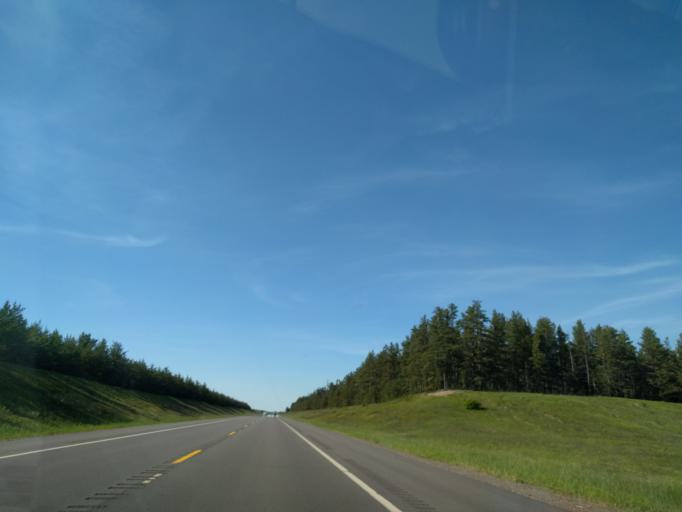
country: US
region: Michigan
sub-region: Marquette County
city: K. I. Sawyer Air Force Base
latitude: 46.3224
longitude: -87.4175
